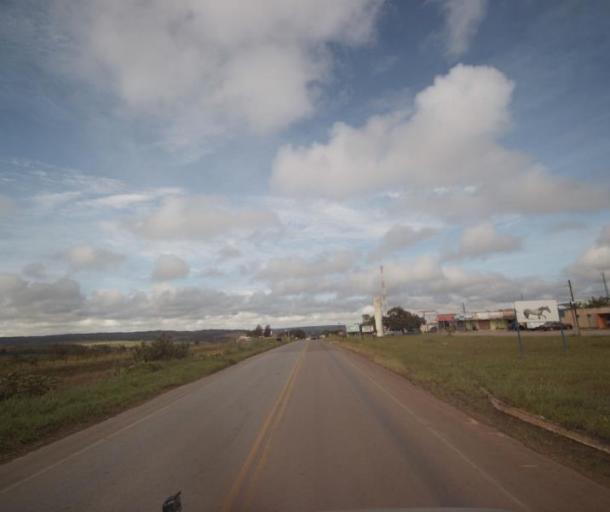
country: BR
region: Goias
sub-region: Pirenopolis
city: Pirenopolis
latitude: -15.7763
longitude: -48.7647
